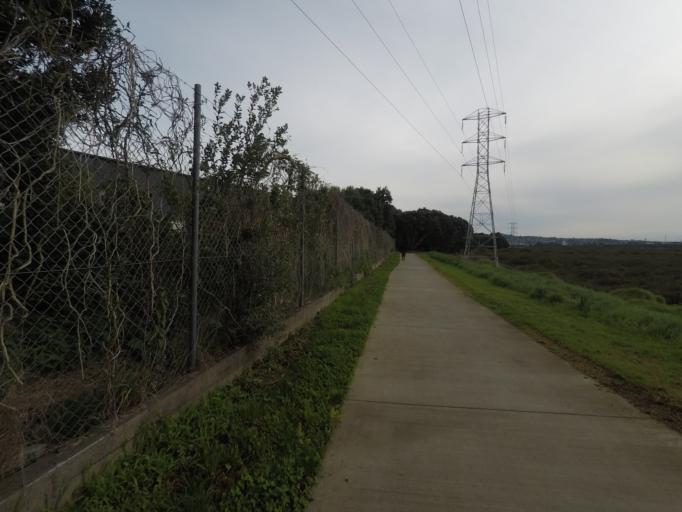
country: NZ
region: Auckland
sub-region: Auckland
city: Mangere
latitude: -36.9463
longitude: 174.7992
